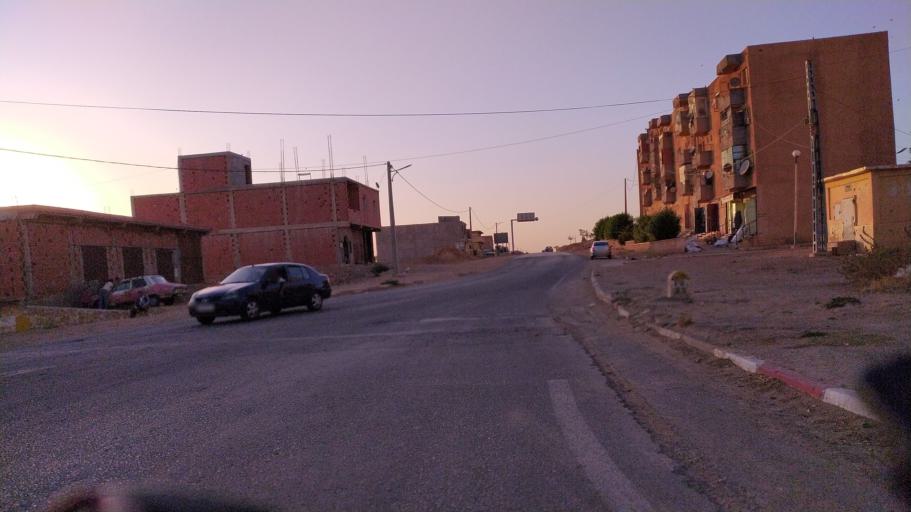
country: DZ
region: Tiaret
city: Frenda
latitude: 34.8974
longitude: 1.2478
